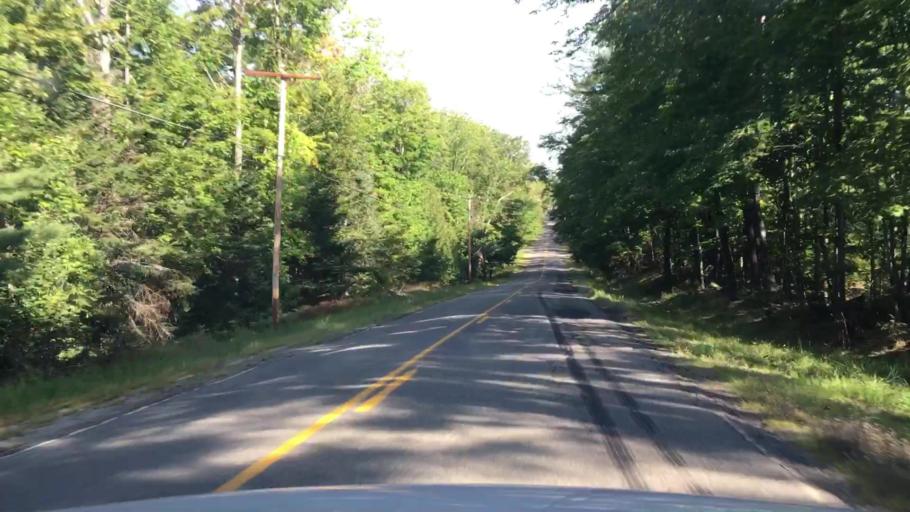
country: US
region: Maine
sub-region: Penobscot County
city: Enfield
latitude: 45.2388
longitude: -68.5532
